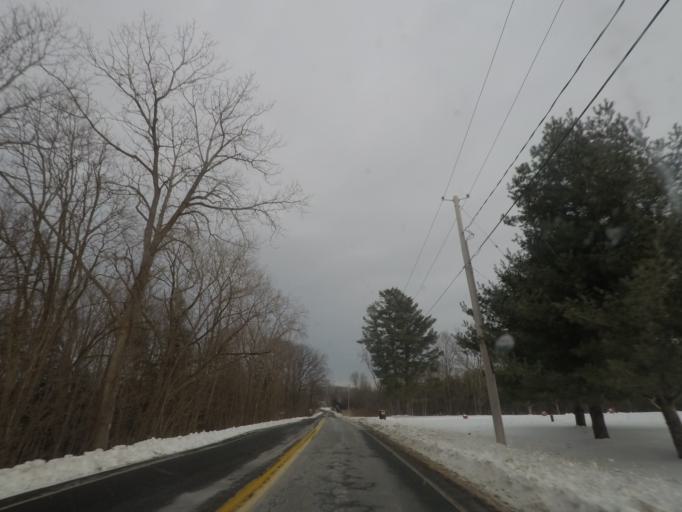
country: US
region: New York
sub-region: Rensselaer County
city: Castleton-on-Hudson
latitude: 42.5148
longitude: -73.7283
